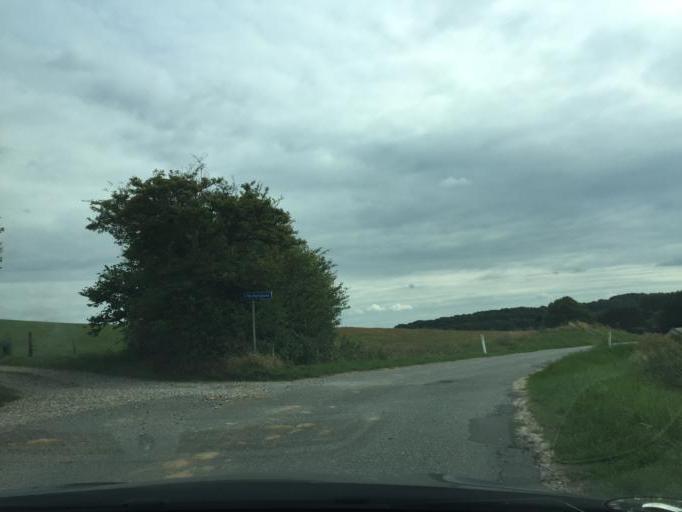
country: DK
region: South Denmark
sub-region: Assens Kommune
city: Vissenbjerg
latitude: 55.3533
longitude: 10.1189
